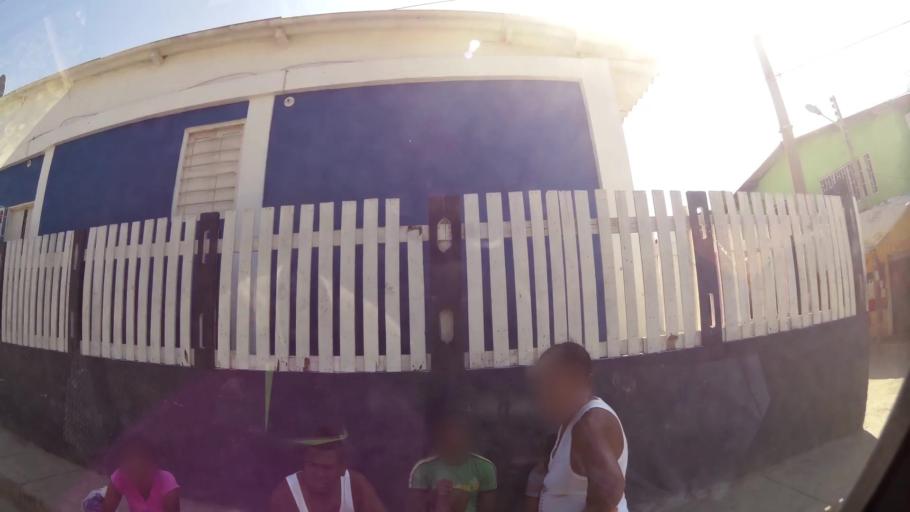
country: CO
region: Bolivar
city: Cartagena
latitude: 10.4134
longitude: -75.5092
